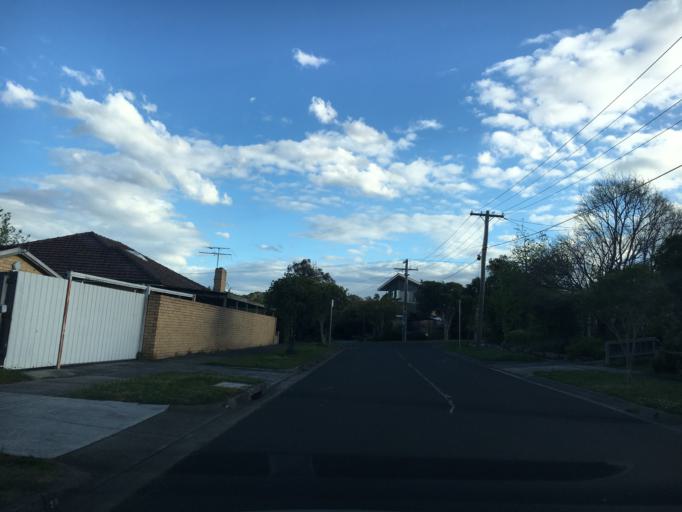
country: AU
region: Victoria
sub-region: Whitehorse
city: Vermont South
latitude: -37.8770
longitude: 145.1731
